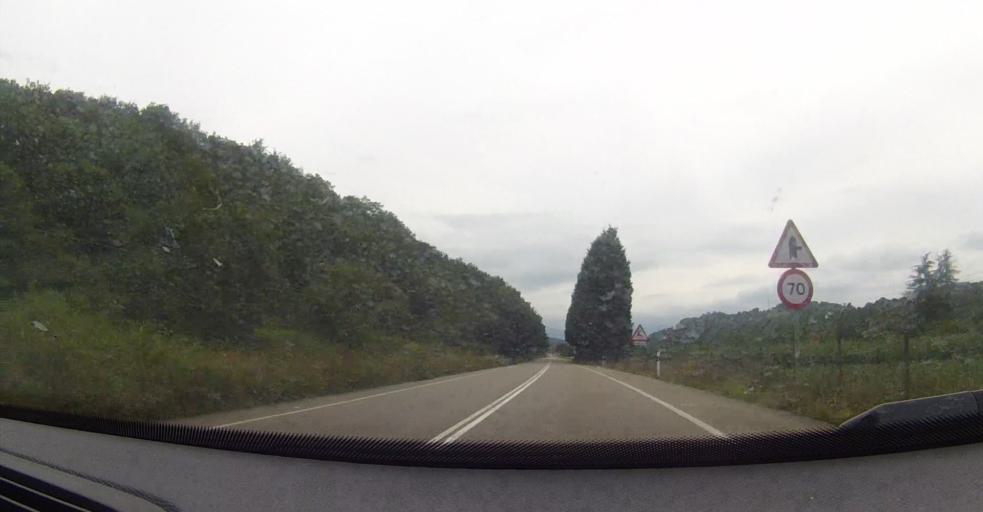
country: ES
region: Asturias
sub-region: Province of Asturias
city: Pilona
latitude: 43.3659
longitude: -5.2943
